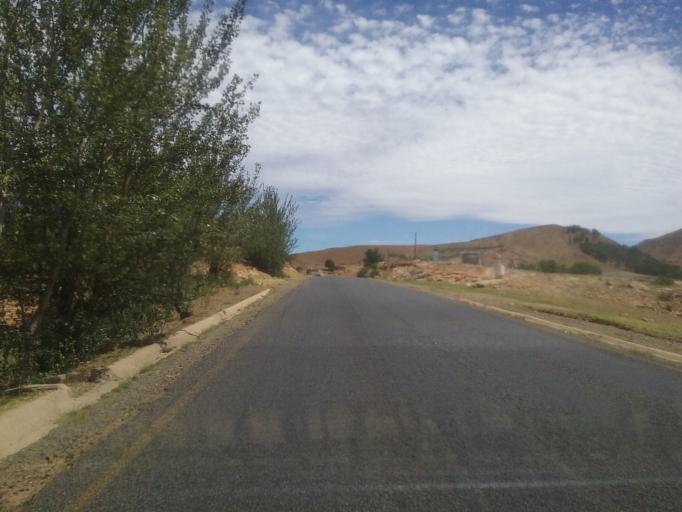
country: LS
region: Mafeteng
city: Mafeteng
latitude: -29.9202
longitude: 27.2511
